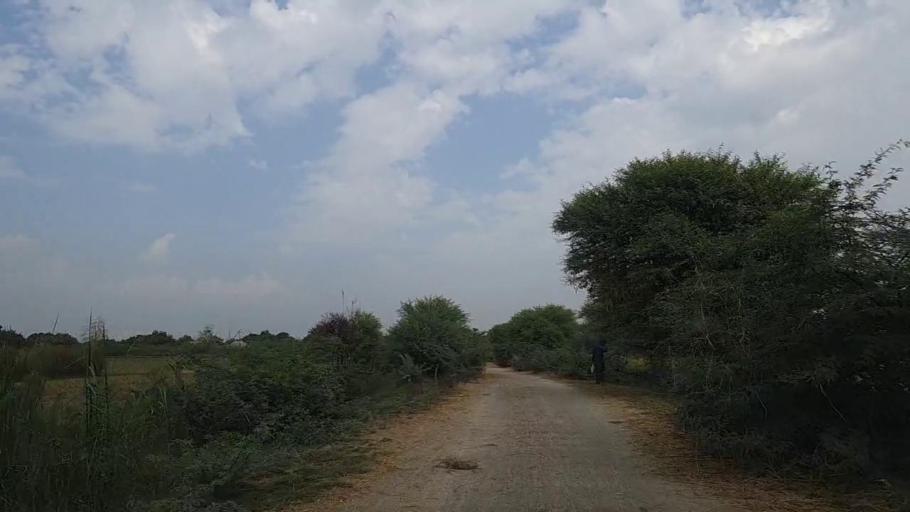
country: PK
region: Sindh
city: Daro Mehar
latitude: 24.7147
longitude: 68.1555
